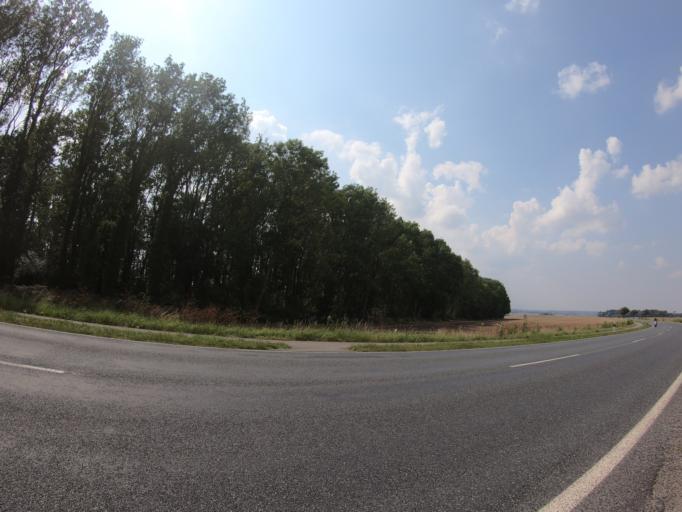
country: DE
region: Lower Saxony
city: Veltheim
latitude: 52.2044
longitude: 10.6815
